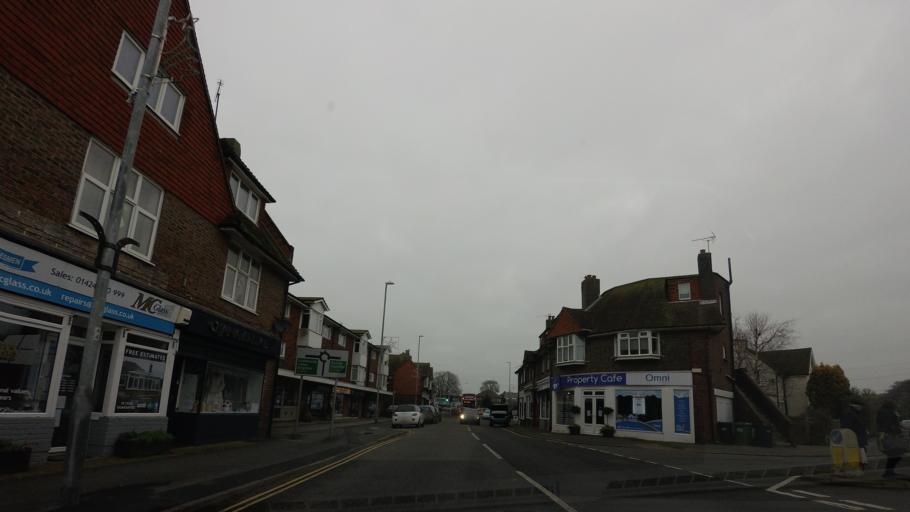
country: GB
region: England
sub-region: East Sussex
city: Bexhill-on-Sea
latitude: 50.8442
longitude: 0.4336
